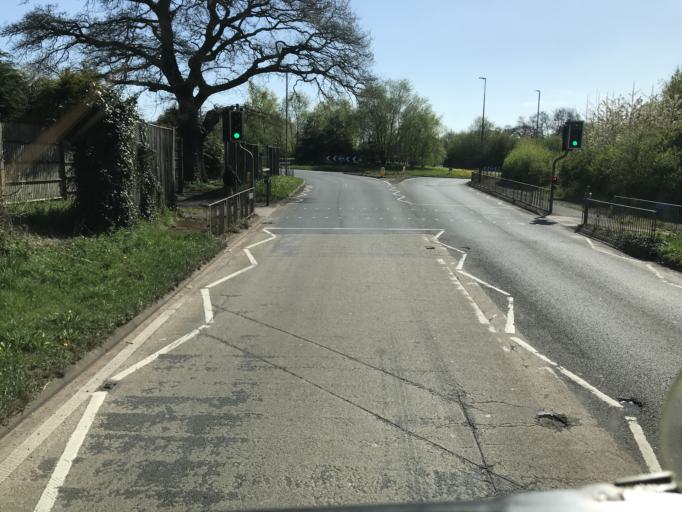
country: GB
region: England
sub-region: Cheshire East
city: Willaston
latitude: 53.0625
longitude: -2.4890
